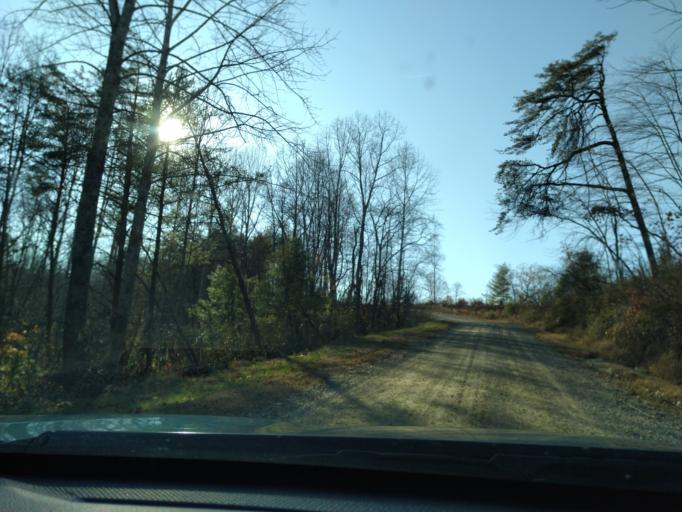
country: US
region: Virginia
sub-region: Floyd County
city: Floyd
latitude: 36.8381
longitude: -80.1925
